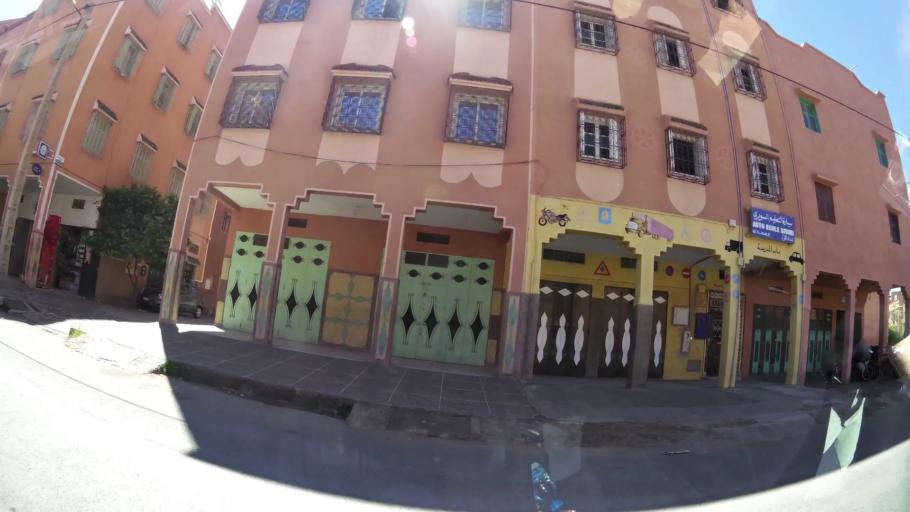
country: MA
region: Marrakech-Tensift-Al Haouz
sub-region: Marrakech
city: Marrakesh
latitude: 31.6357
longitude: -8.0653
